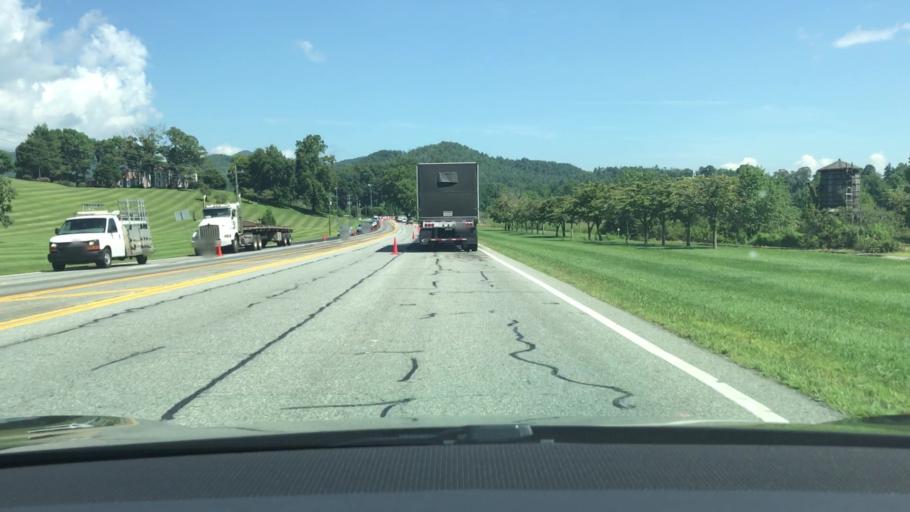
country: US
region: Georgia
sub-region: Rabun County
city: Mountain City
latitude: 34.9590
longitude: -83.3868
